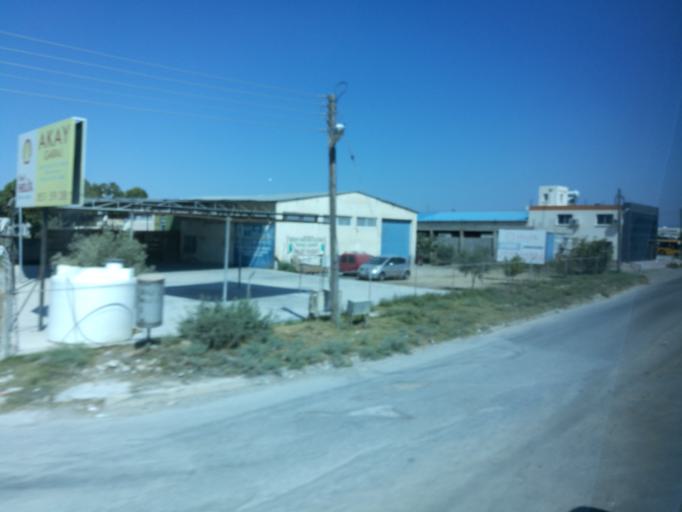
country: CY
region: Ammochostos
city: Famagusta
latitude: 35.1470
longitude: 33.9030
